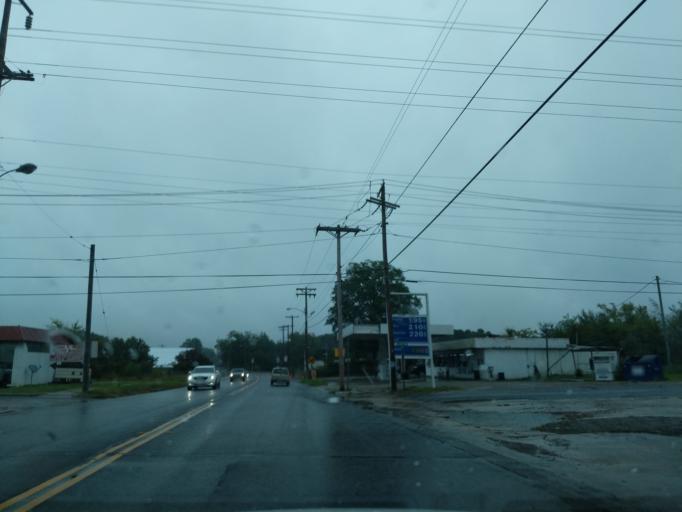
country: US
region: Texas
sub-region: Panola County
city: Carthage
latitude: 32.1569
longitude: -94.3364
